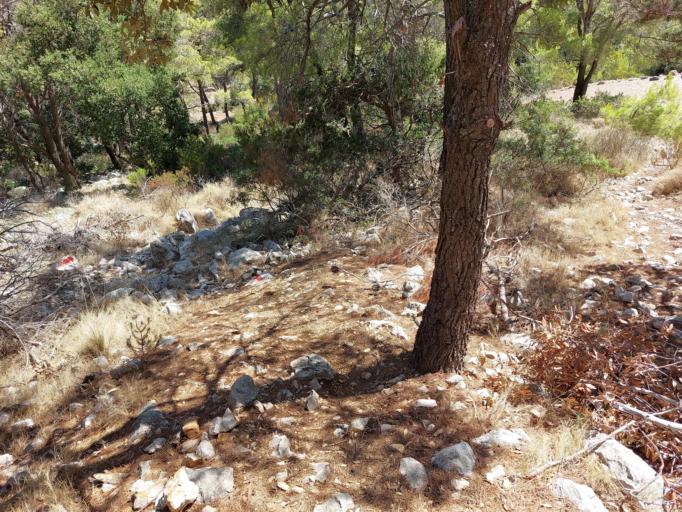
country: HR
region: Dubrovacko-Neretvanska
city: Smokvica
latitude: 42.7424
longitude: 16.8376
